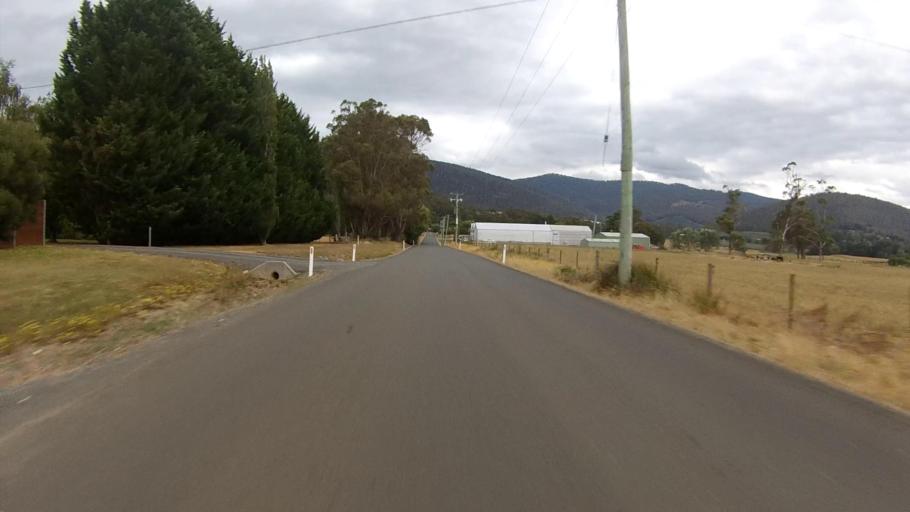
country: AU
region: Tasmania
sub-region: Huon Valley
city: Huonville
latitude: -42.9767
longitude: 147.0948
